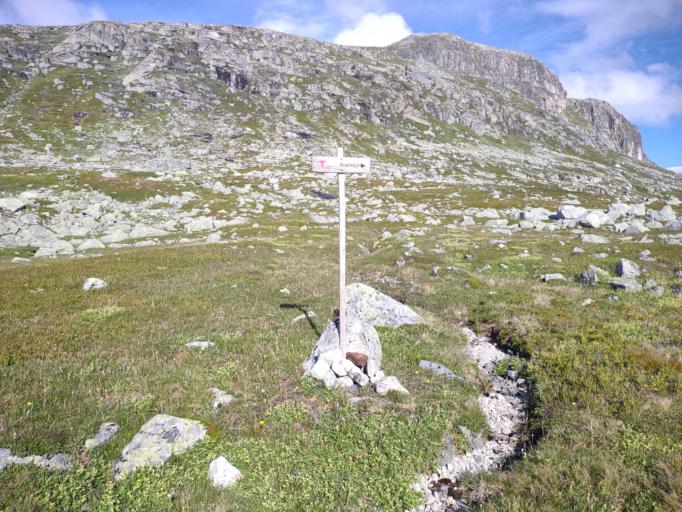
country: NO
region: Hordaland
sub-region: Eidfjord
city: Eidfjord
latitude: 60.4972
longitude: 7.6317
